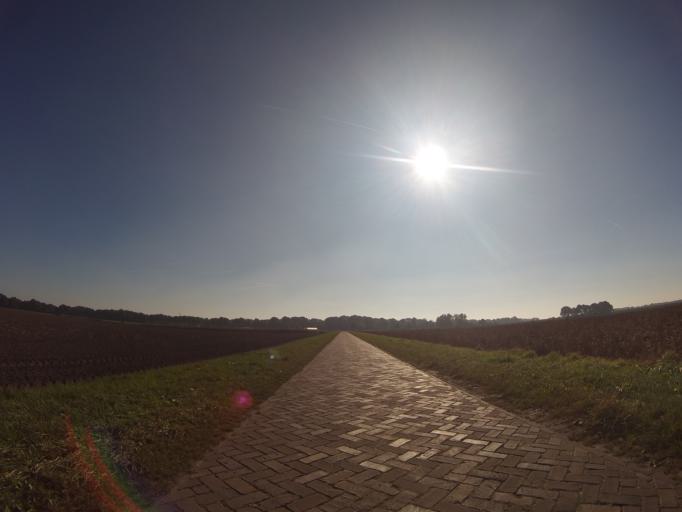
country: NL
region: Drenthe
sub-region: Gemeente Coevorden
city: Dalen
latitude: 52.7657
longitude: 6.7128
